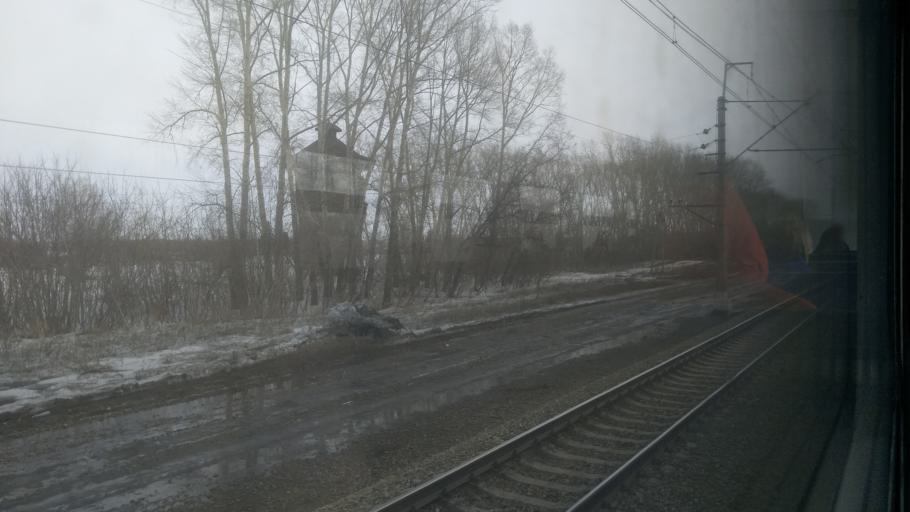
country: RU
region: Kemerovo
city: Yurga
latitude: 55.6983
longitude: 84.6546
